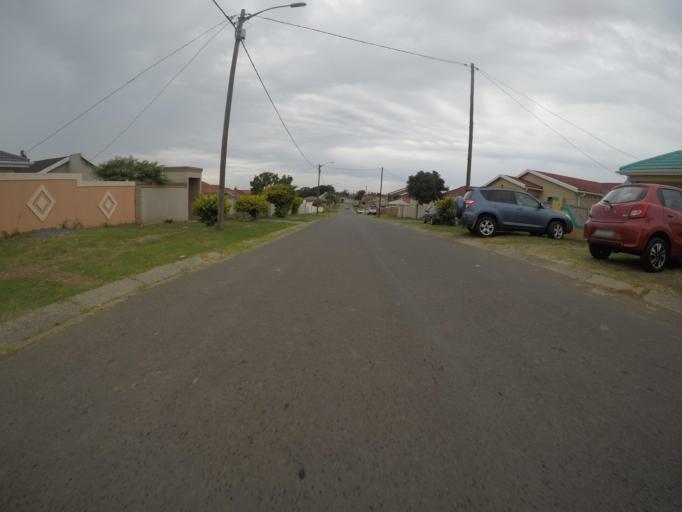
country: ZA
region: Eastern Cape
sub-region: Buffalo City Metropolitan Municipality
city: East London
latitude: -32.9950
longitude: 27.8462
